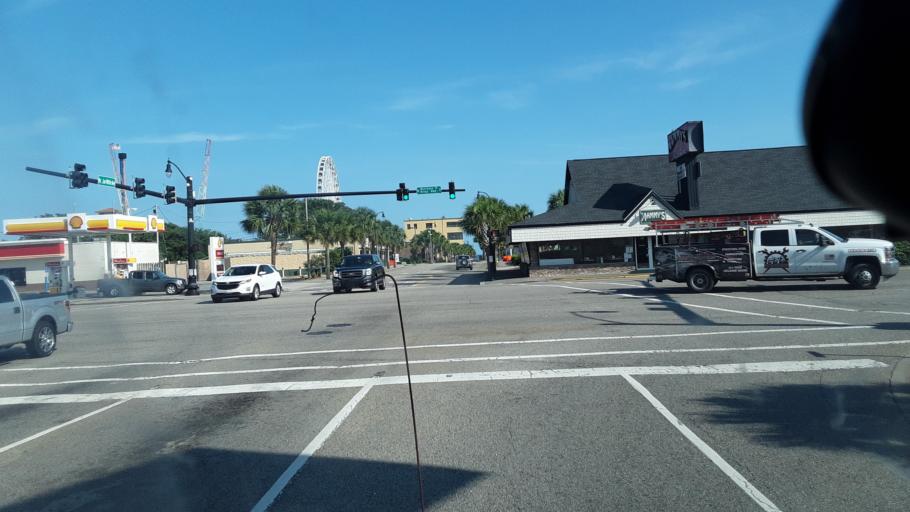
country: US
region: South Carolina
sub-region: Horry County
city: Myrtle Beach
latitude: 33.6957
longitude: -78.8805
